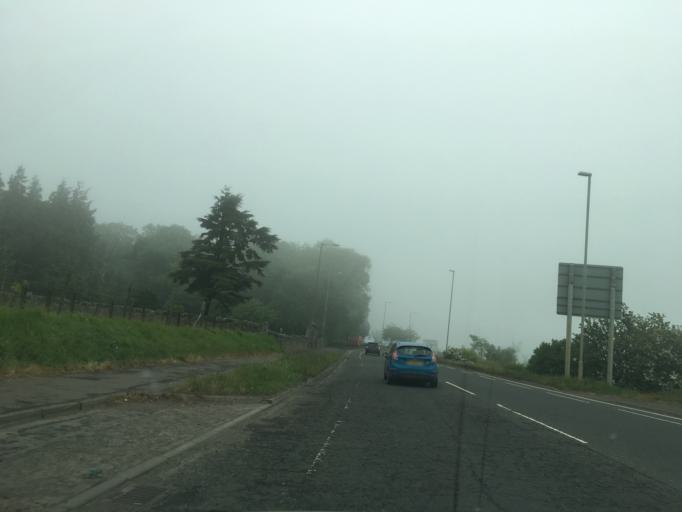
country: GB
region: Scotland
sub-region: Midlothian
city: Loanhead
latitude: 55.8546
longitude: -3.1892
